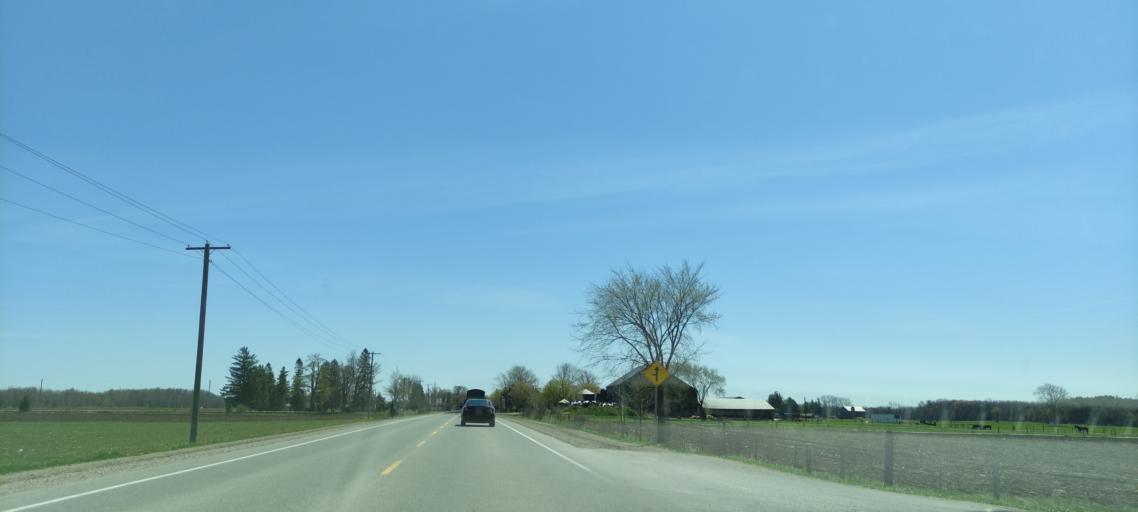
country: CA
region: Ontario
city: Waterloo
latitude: 43.5818
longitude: -80.4256
